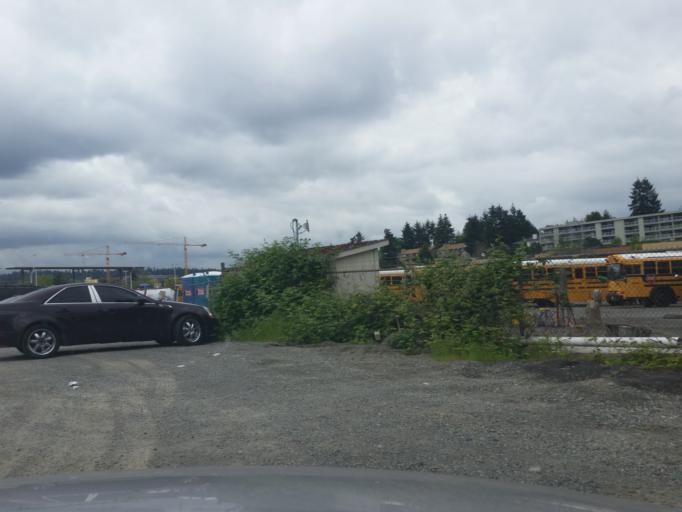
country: US
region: Washington
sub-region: King County
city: Bellevue
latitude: 47.6143
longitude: -122.1820
